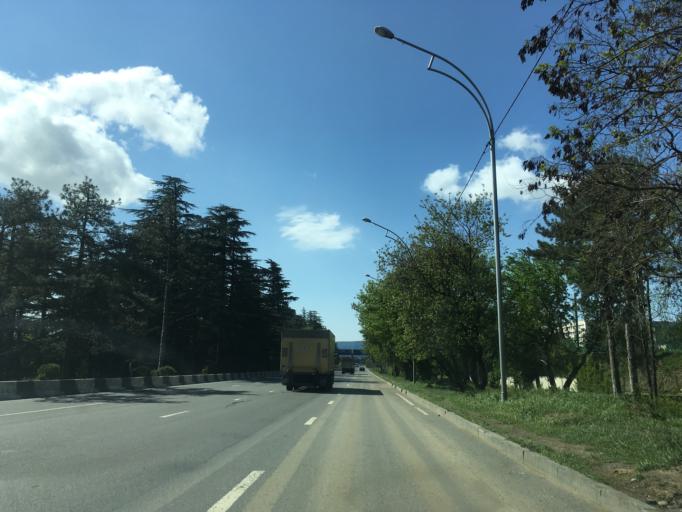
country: GE
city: Zahesi
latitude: 41.8103
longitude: 44.7713
